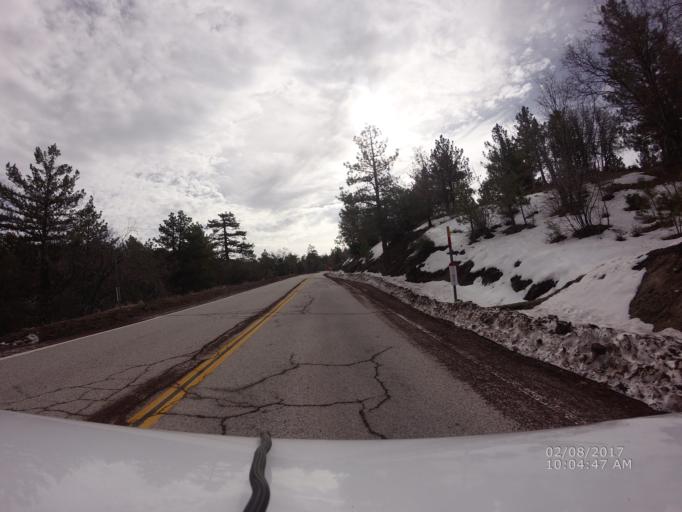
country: US
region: California
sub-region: San Bernardino County
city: Pinon Hills
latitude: 34.3993
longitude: -117.7336
